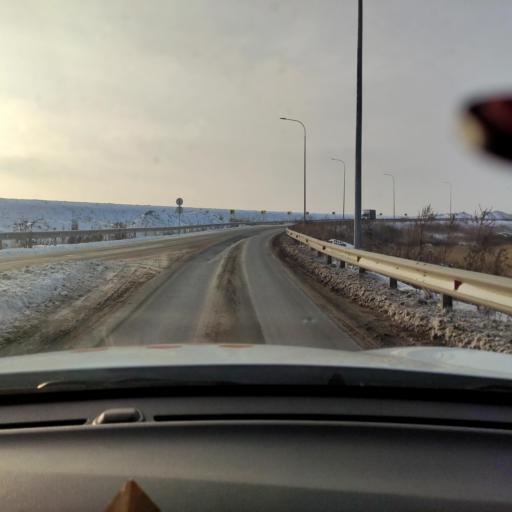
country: RU
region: Tatarstan
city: Sviyazhsk
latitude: 55.7404
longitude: 48.7826
